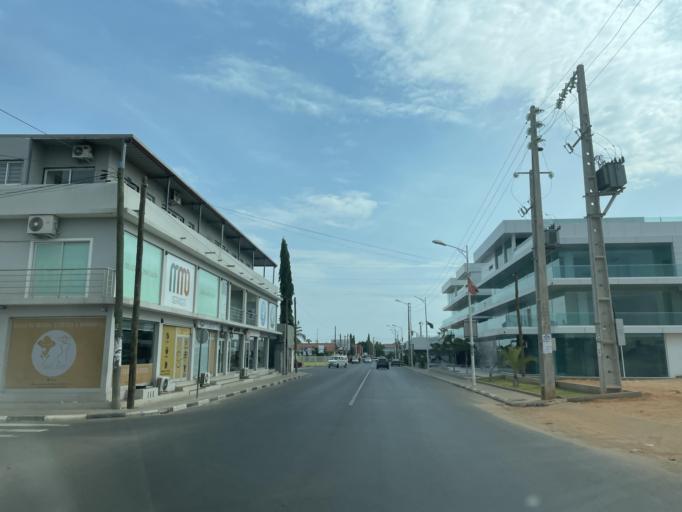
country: AO
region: Luanda
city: Luanda
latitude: -8.9477
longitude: 13.1881
